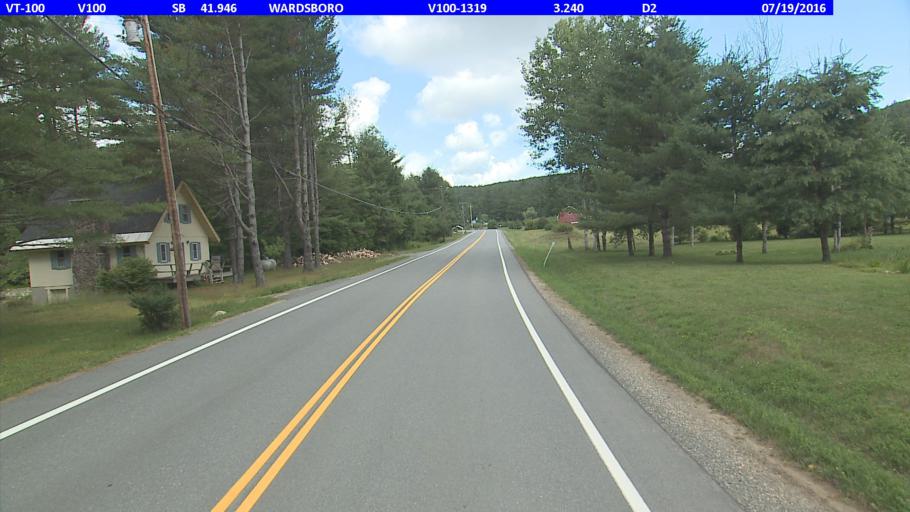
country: US
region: Vermont
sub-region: Windham County
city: Dover
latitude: 43.0444
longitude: -72.8570
